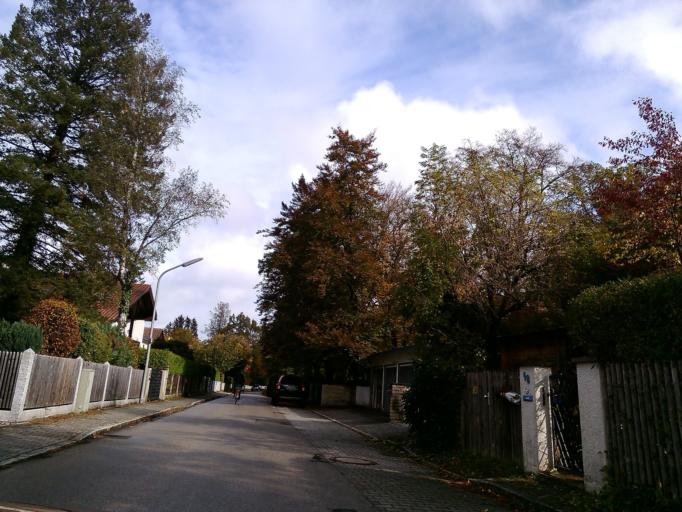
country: DE
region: Bavaria
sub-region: Upper Bavaria
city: Gauting
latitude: 48.0726
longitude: 11.3810
